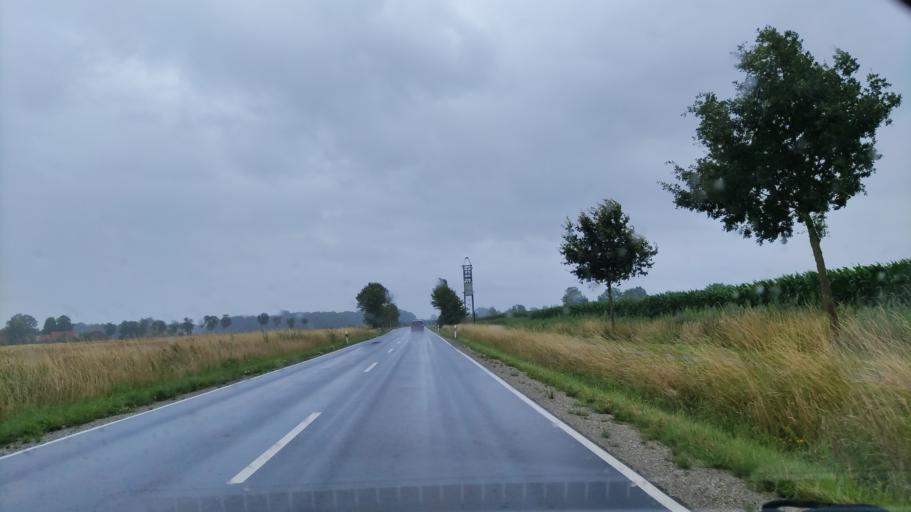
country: DE
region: North Rhine-Westphalia
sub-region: Regierungsbezirk Munster
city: Everswinkel
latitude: 51.9028
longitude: 7.8235
